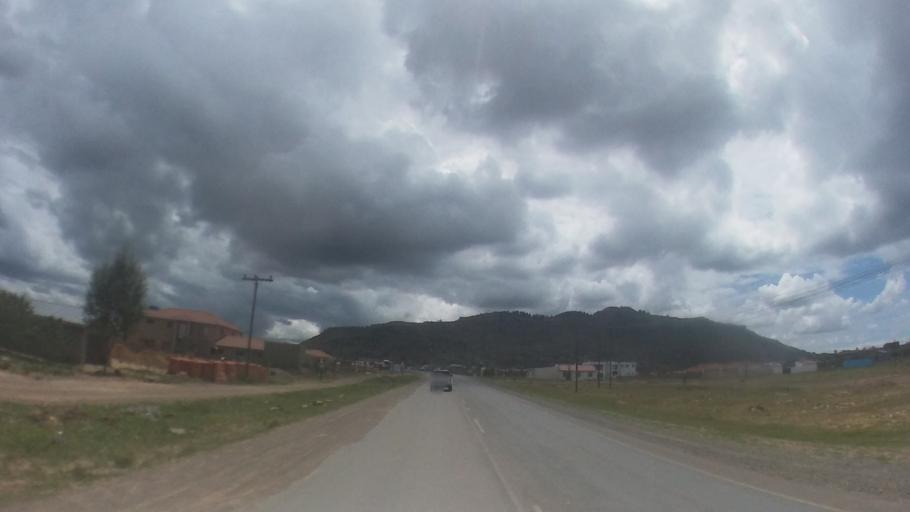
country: LS
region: Maseru
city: Maseru
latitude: -29.3701
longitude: 27.4709
